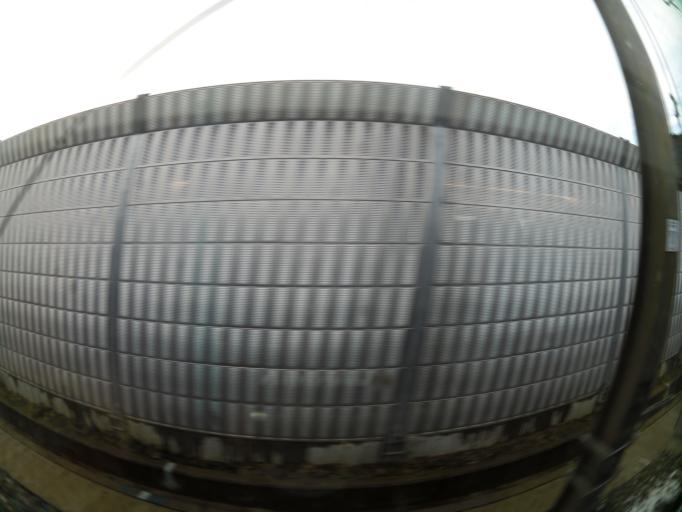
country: KR
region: Daejeon
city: Daejeon
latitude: 36.3263
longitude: 127.4371
